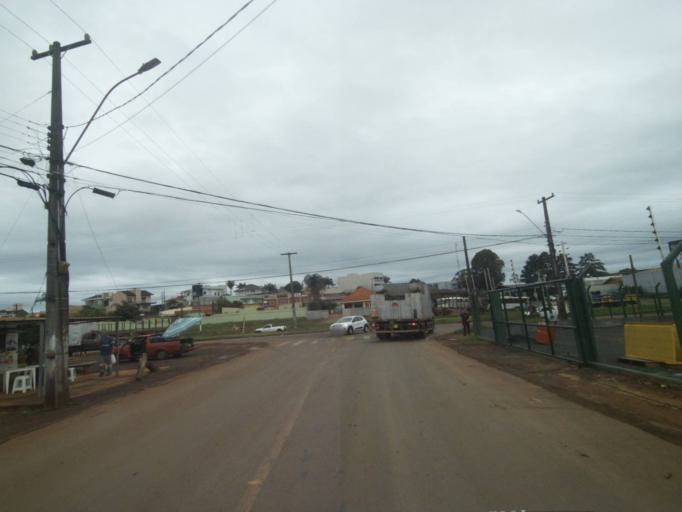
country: BR
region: Parana
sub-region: Telemaco Borba
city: Telemaco Borba
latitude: -24.3313
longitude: -50.6486
